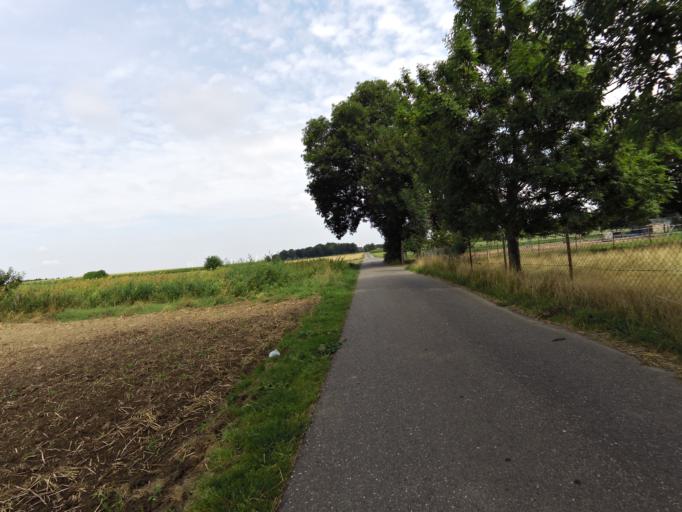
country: DE
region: North Rhine-Westphalia
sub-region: Regierungsbezirk Koln
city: Gangelt
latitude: 50.9990
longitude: 6.0439
